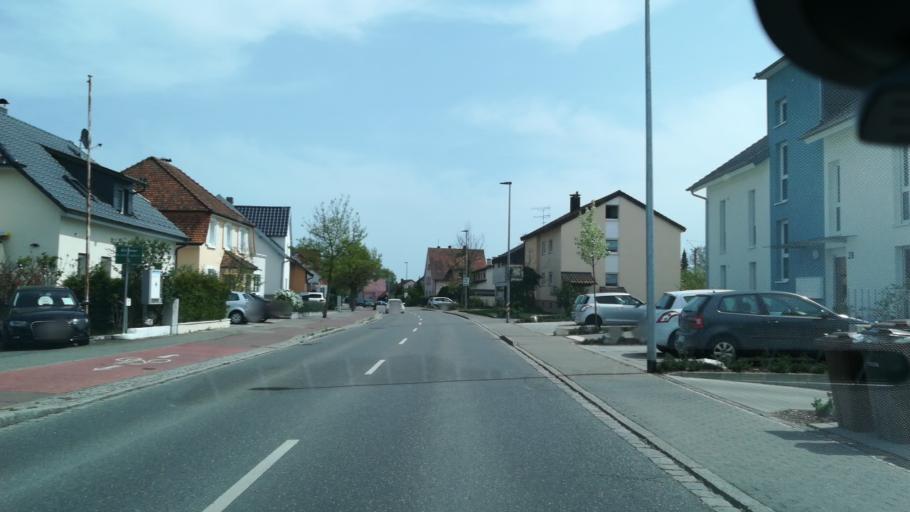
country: DE
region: Baden-Wuerttemberg
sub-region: Freiburg Region
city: Moos
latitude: 47.7525
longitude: 8.9408
